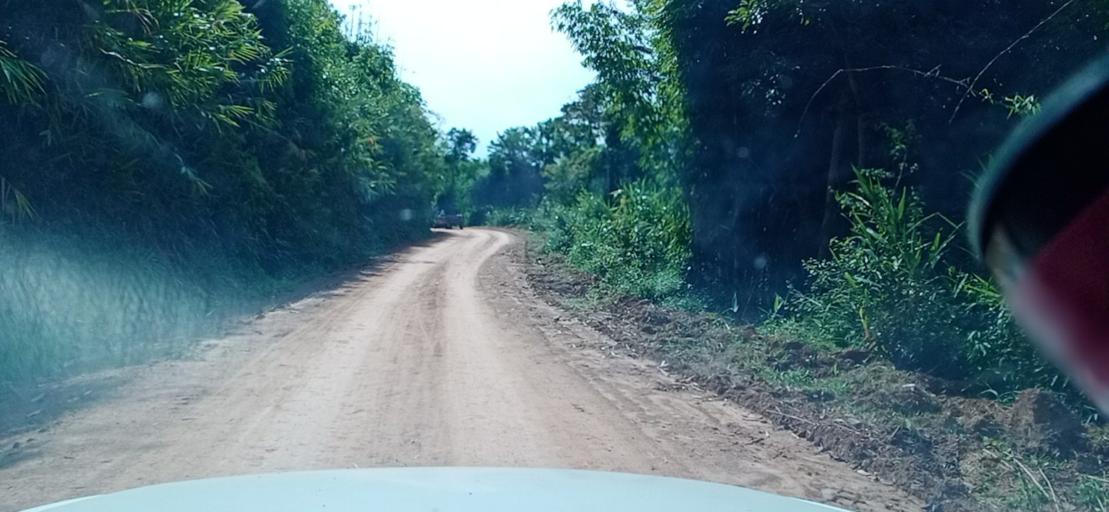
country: TH
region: Changwat Bueng Kan
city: Pak Khat
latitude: 18.6373
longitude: 103.2484
